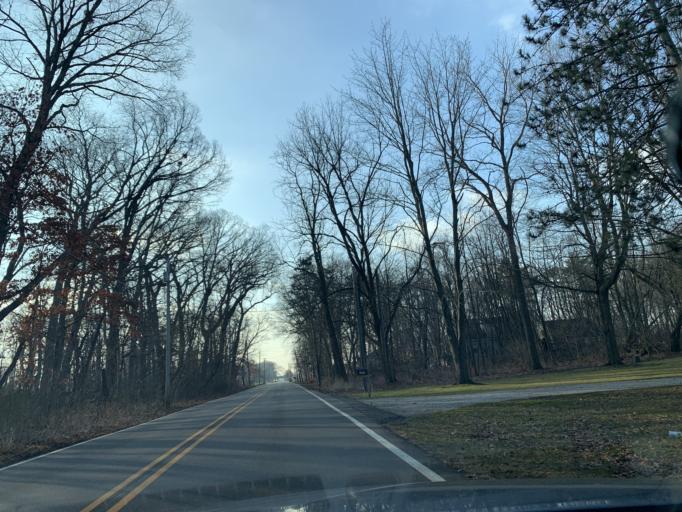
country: US
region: Indiana
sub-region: Porter County
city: Portage
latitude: 41.5807
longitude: -87.1535
